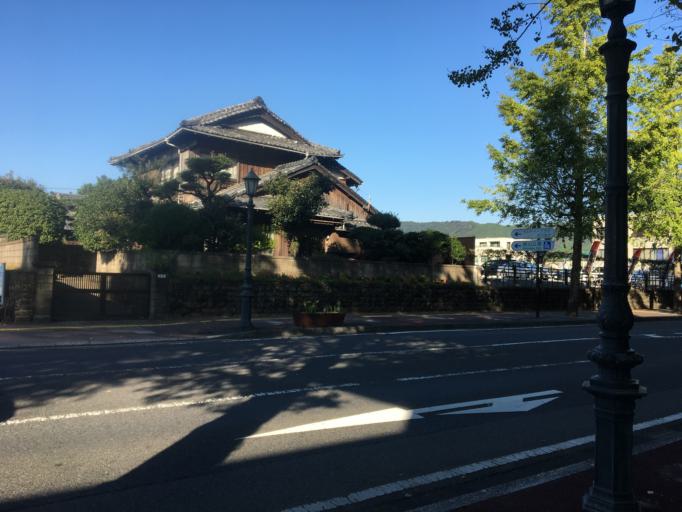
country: JP
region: Miyazaki
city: Nobeoka
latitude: 32.5819
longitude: 131.6646
